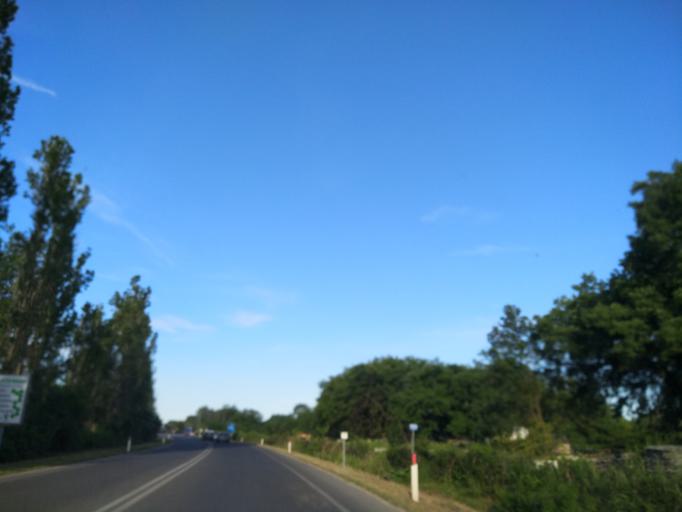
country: IT
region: The Marches
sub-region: Provincia di Pesaro e Urbino
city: Pesaro
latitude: 43.8869
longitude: 12.8649
